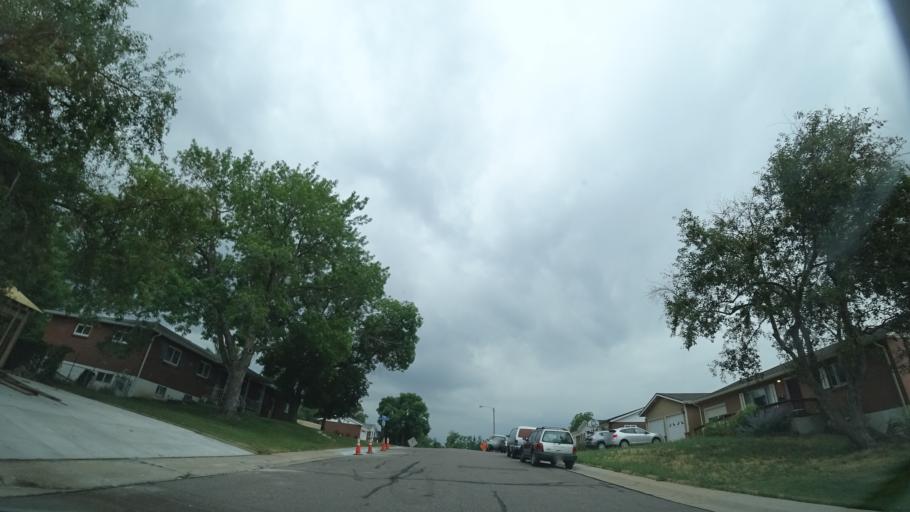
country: US
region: Colorado
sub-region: Jefferson County
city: Lakewood
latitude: 39.7017
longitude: -105.1295
